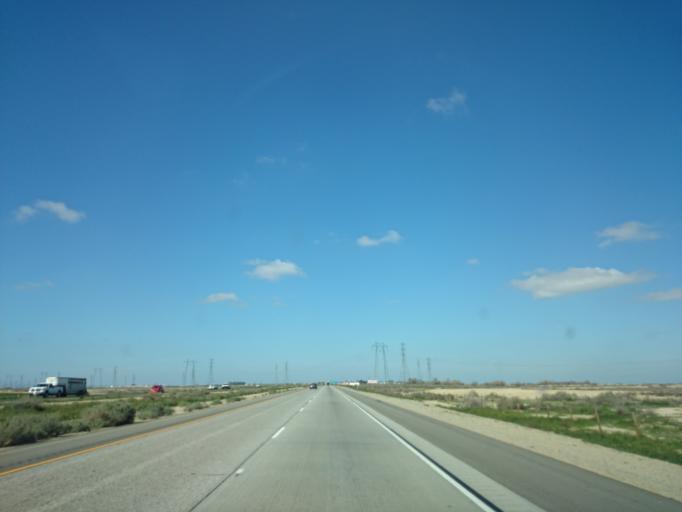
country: US
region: California
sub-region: Kern County
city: Buttonwillow
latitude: 35.3832
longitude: -119.3754
